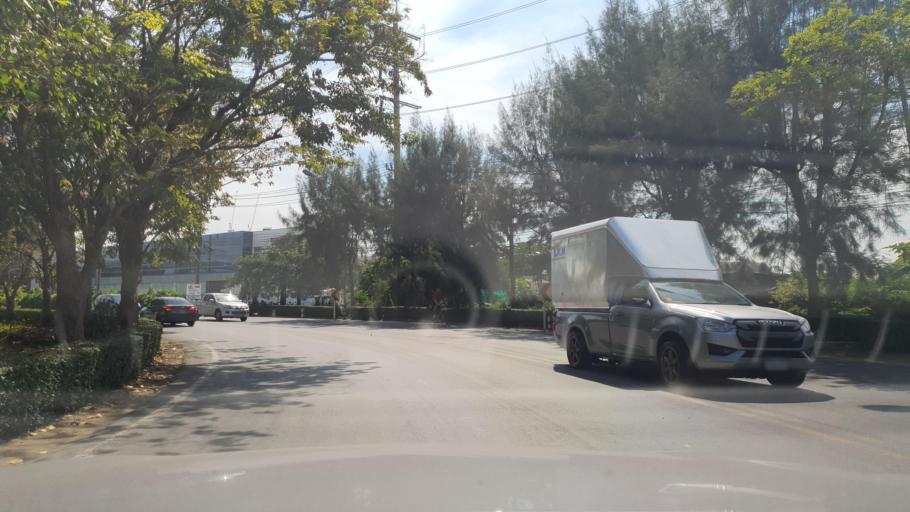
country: TH
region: Bangkok
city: Bang Na
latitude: 13.6626
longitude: 100.6427
